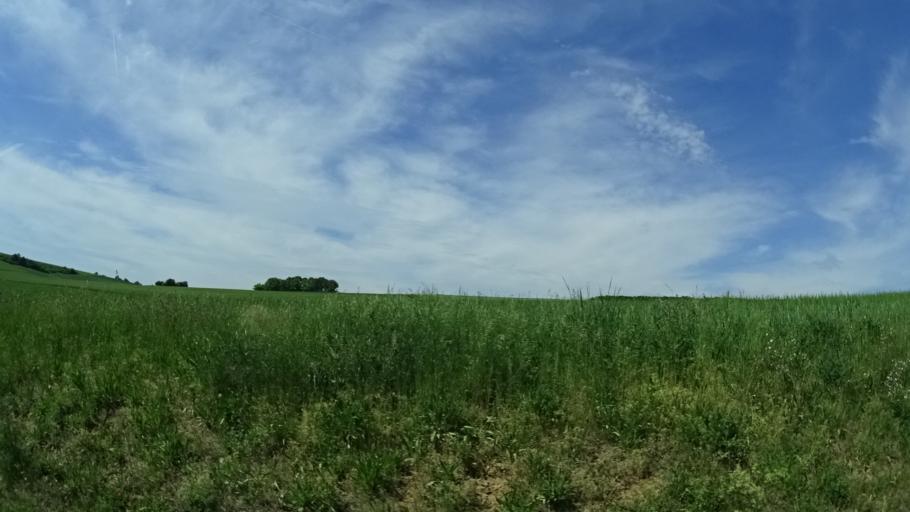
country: DE
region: Bavaria
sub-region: Regierungsbezirk Unterfranken
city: Wasserlosen
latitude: 50.0300
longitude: 10.0200
